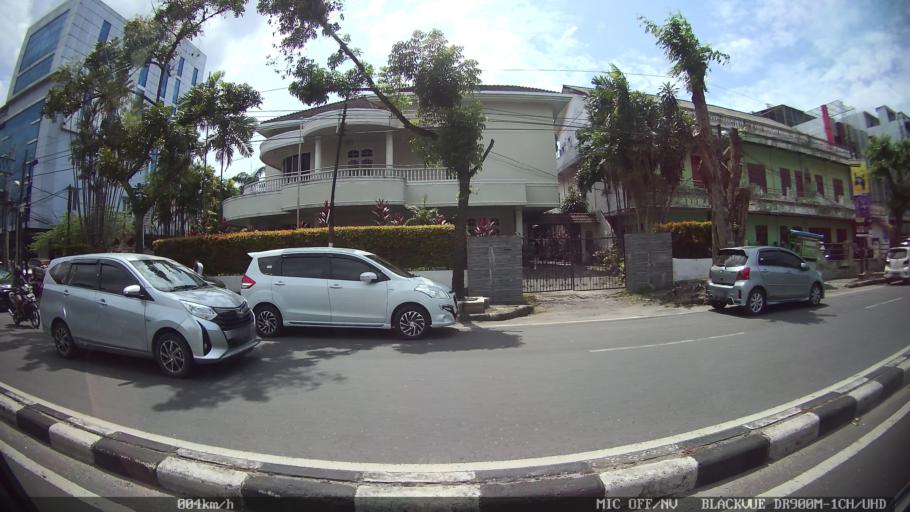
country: ID
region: North Sumatra
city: Medan
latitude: 3.5745
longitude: 98.6610
